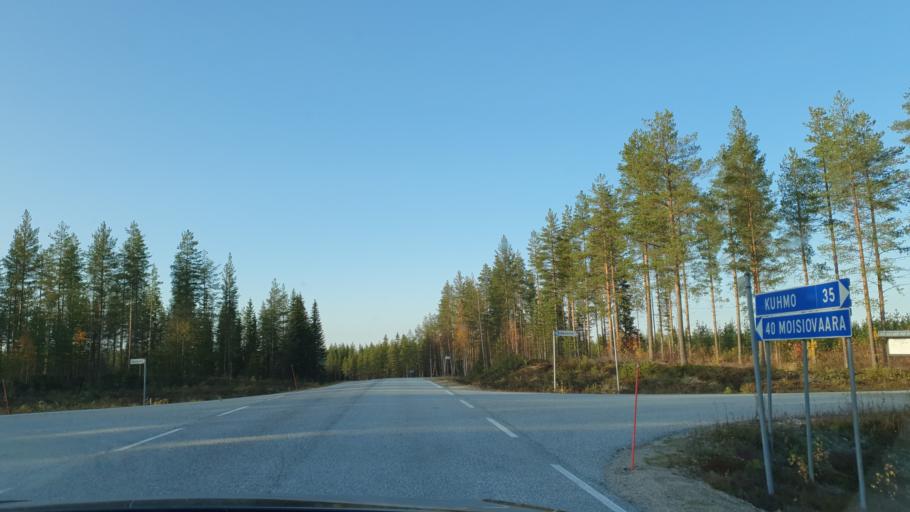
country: FI
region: Kainuu
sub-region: Kehys-Kainuu
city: Kuhmo
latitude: 64.3724
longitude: 29.4893
